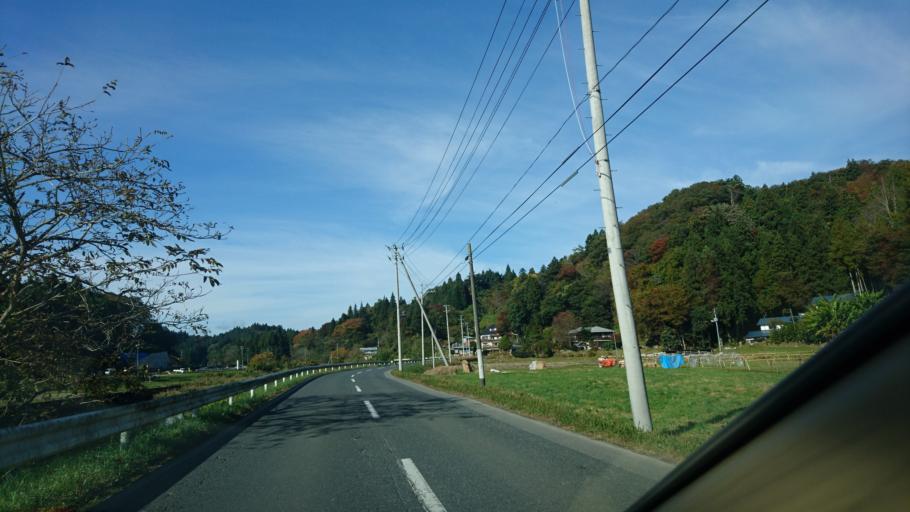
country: JP
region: Iwate
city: Ichinoseki
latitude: 39.0160
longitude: 141.3740
